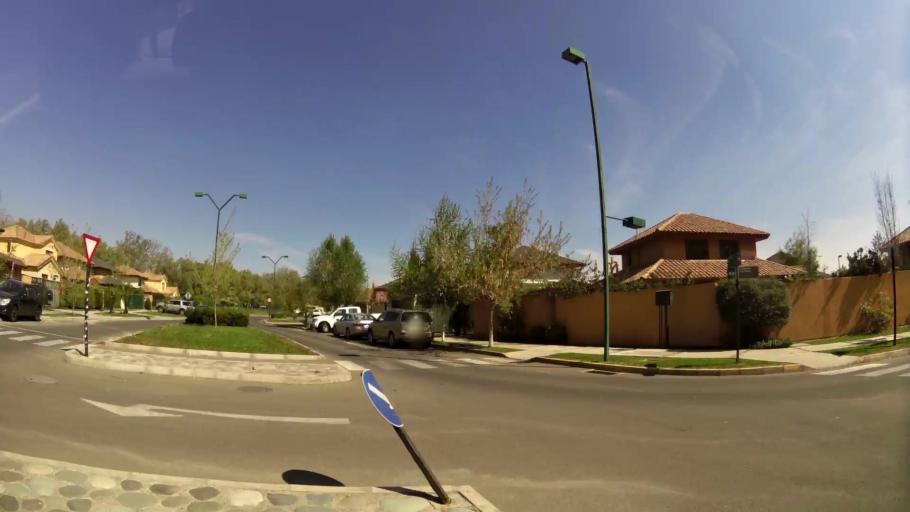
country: CL
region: Santiago Metropolitan
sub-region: Provincia de Santiago
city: Villa Presidente Frei, Nunoa, Santiago, Chile
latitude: -33.4888
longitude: -70.5682
